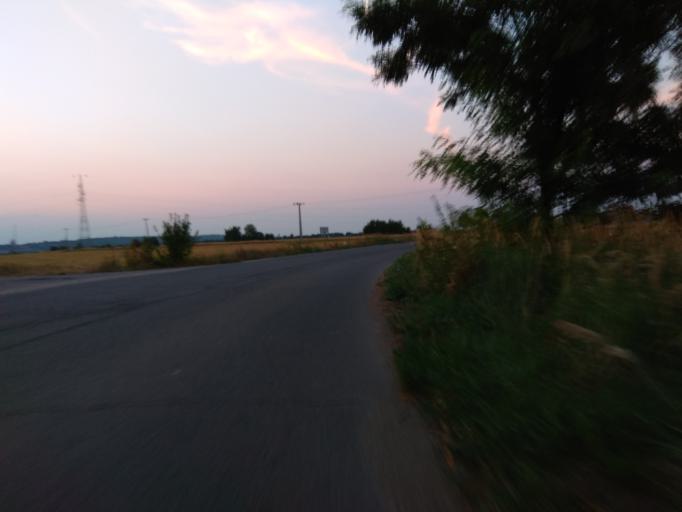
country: HU
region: Borsod-Abauj-Zemplen
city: Emod
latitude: 47.9223
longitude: 20.8395
